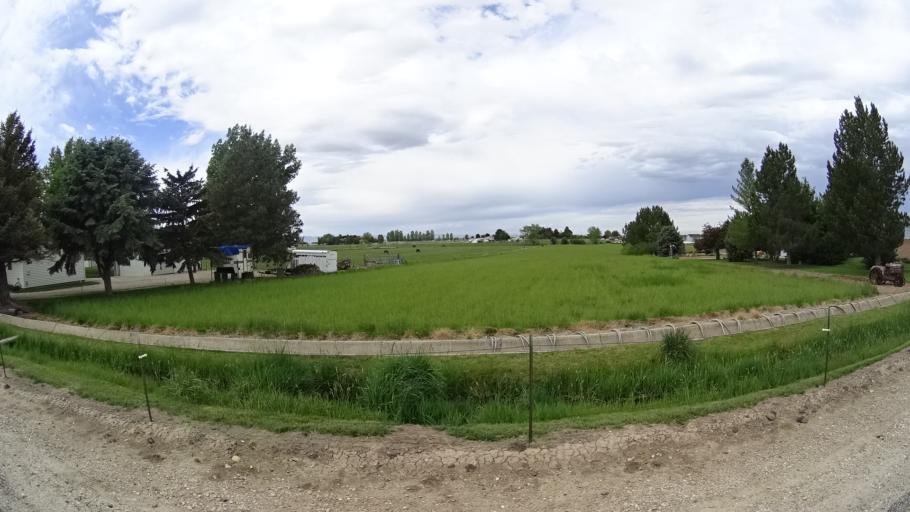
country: US
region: Idaho
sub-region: Ada County
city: Kuna
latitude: 43.4762
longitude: -116.4336
